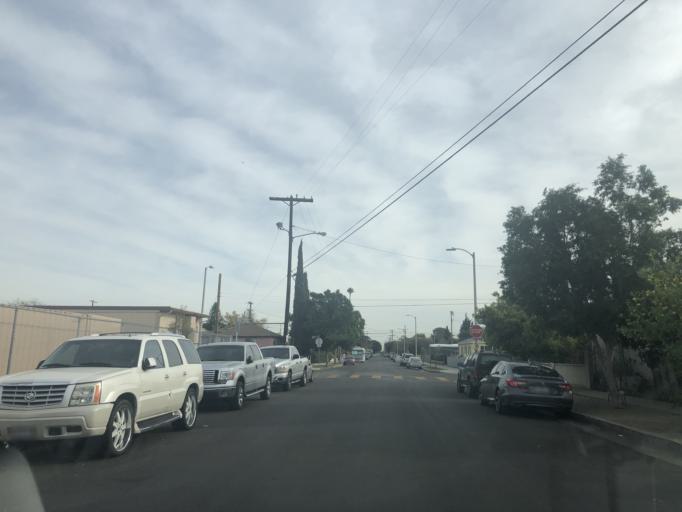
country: US
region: California
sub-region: Los Angeles County
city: San Fernando
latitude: 34.2673
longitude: -118.4324
